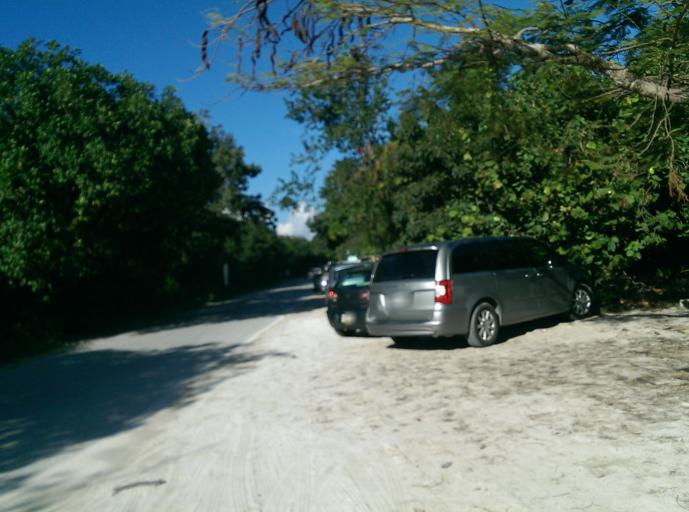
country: MX
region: Quintana Roo
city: Tulum
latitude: 20.2027
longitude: -87.4343
